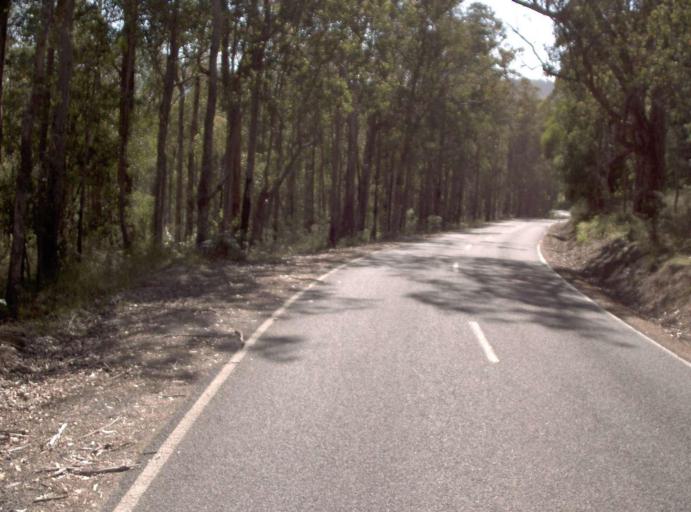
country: AU
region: New South Wales
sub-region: Bombala
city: Bombala
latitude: -37.3788
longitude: 148.6657
